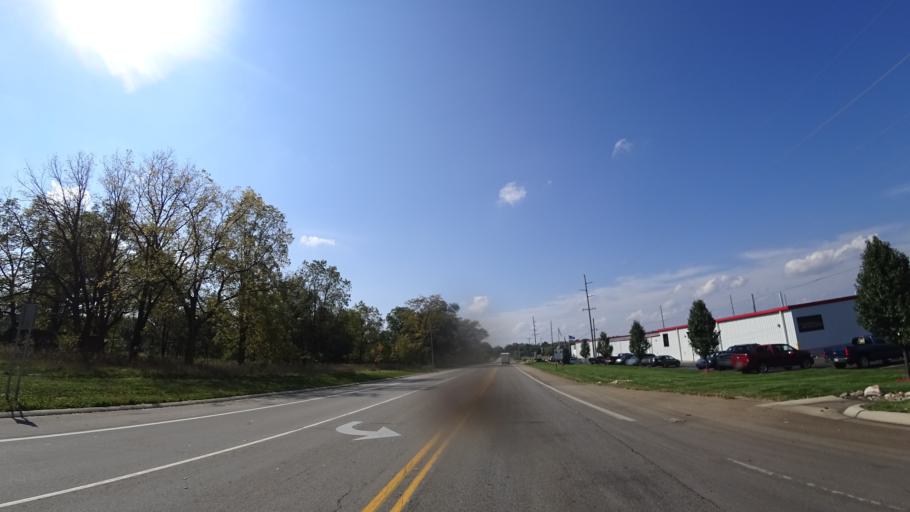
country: US
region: Michigan
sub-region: Jackson County
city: Concord
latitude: 42.1630
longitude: -84.7118
